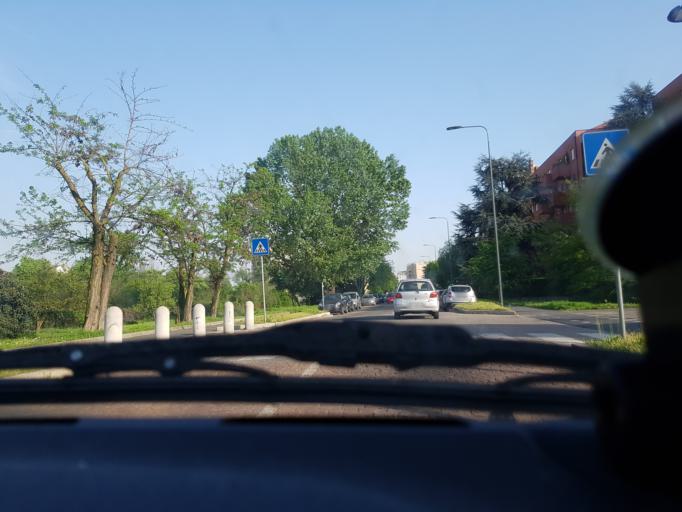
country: IT
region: Lombardy
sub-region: Citta metropolitana di Milano
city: Cesano Boscone
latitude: 45.4565
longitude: 9.0990
